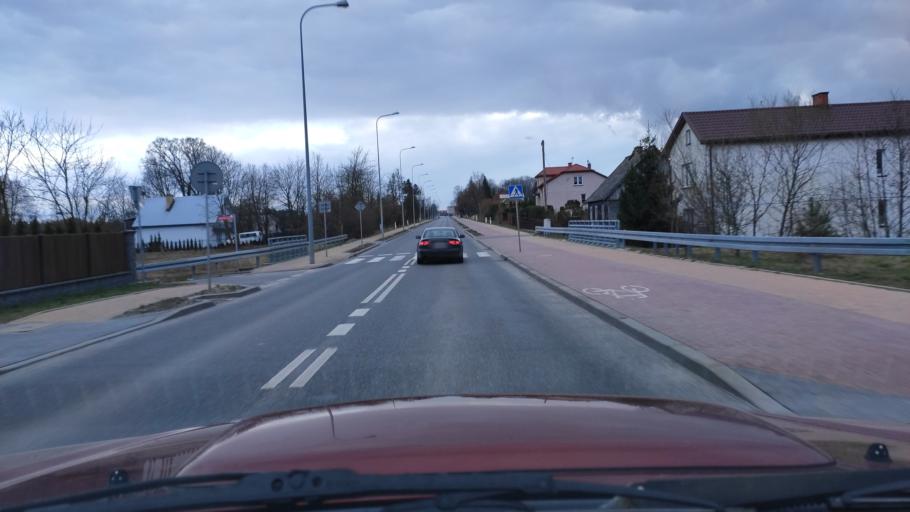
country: PL
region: Masovian Voivodeship
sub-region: Powiat zwolenski
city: Zwolen
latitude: 51.3662
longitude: 21.5847
